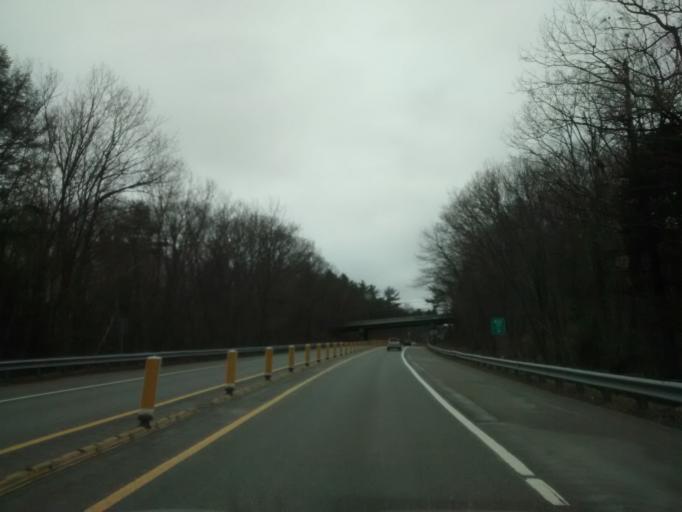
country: US
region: Massachusetts
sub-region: Worcester County
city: Phillipston
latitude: 42.5722
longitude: -72.1522
